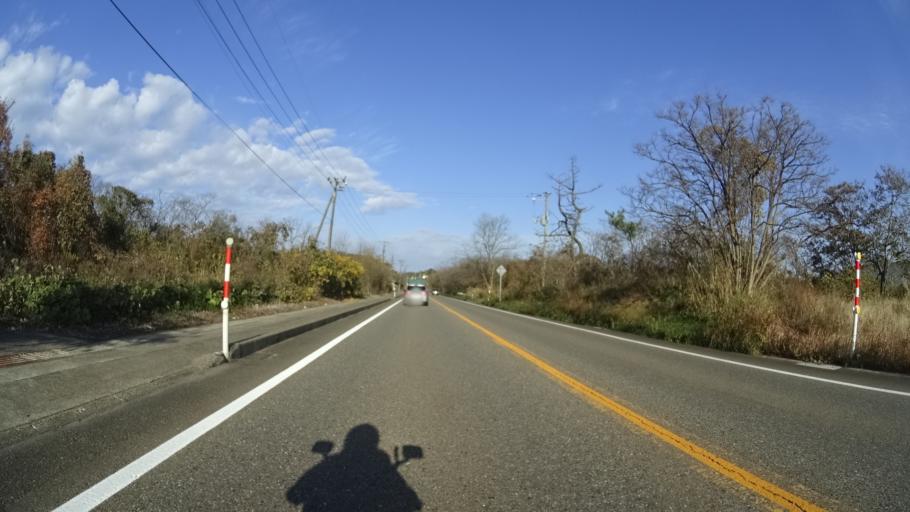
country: JP
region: Niigata
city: Joetsu
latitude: 37.2601
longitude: 138.3699
